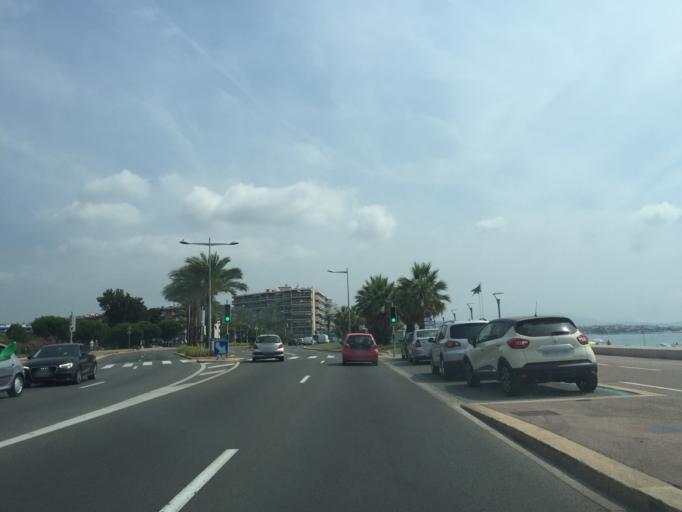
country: FR
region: Provence-Alpes-Cote d'Azur
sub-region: Departement des Alpes-Maritimes
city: Cagnes-sur-Mer
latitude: 43.6494
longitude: 7.1506
